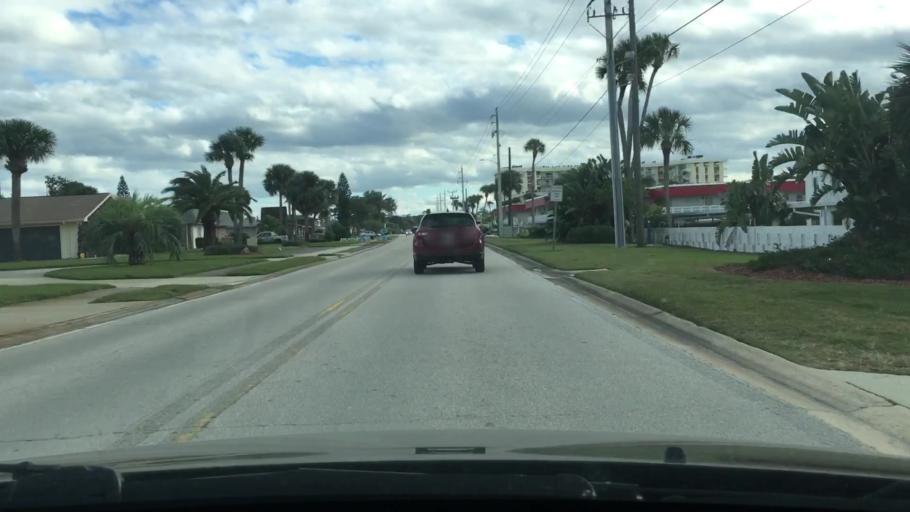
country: US
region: Florida
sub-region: Volusia County
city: Holly Hill
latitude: 29.2652
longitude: -81.0356
